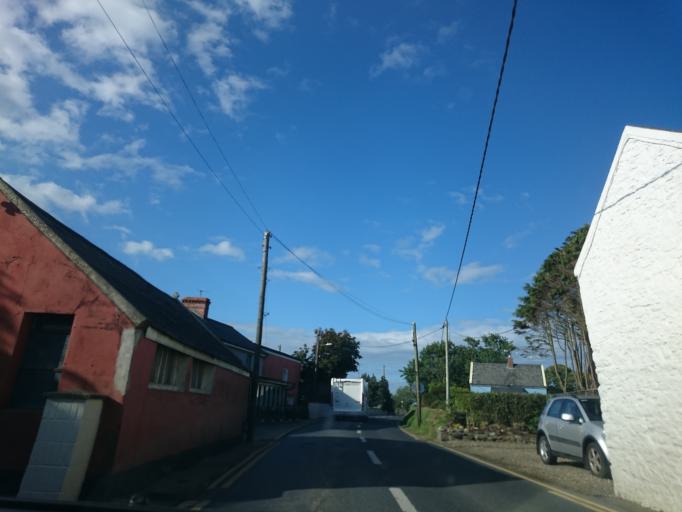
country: IE
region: Leinster
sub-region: Loch Garman
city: Loch Garman
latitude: 52.2048
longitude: -6.5486
